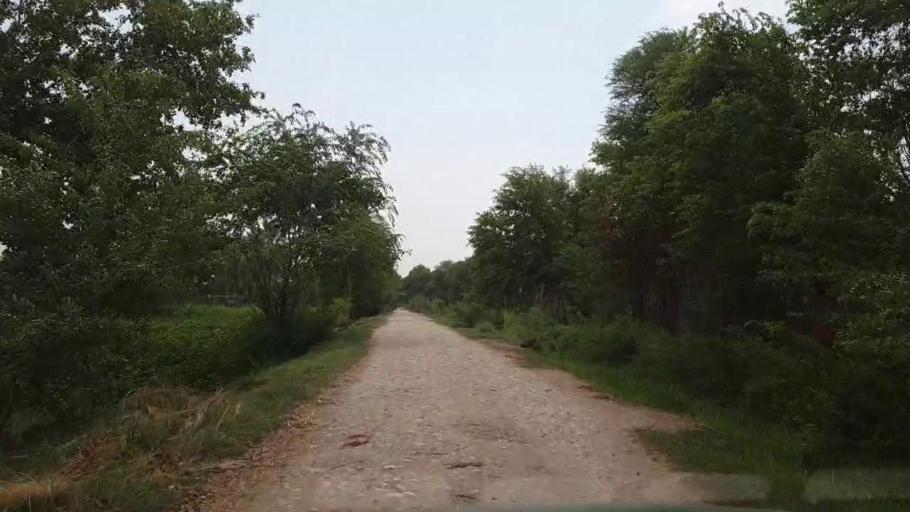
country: PK
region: Sindh
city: Pir jo Goth
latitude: 27.4905
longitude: 68.5960
